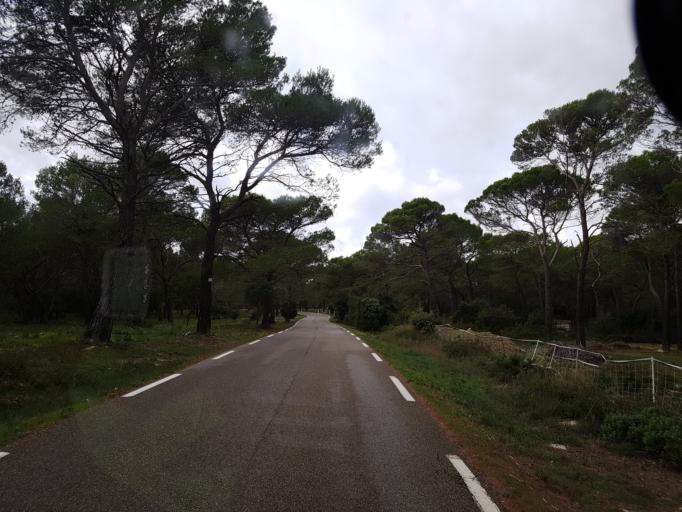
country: FR
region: Provence-Alpes-Cote d'Azur
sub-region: Departement des Bouches-du-Rhone
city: Cuges-les-Pins
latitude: 43.2522
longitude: 5.7365
